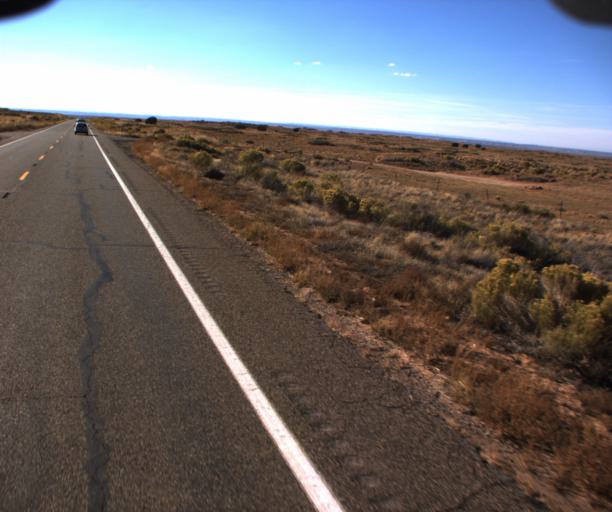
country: US
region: Arizona
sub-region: Coconino County
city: Kaibito
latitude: 36.6156
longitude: -110.9876
